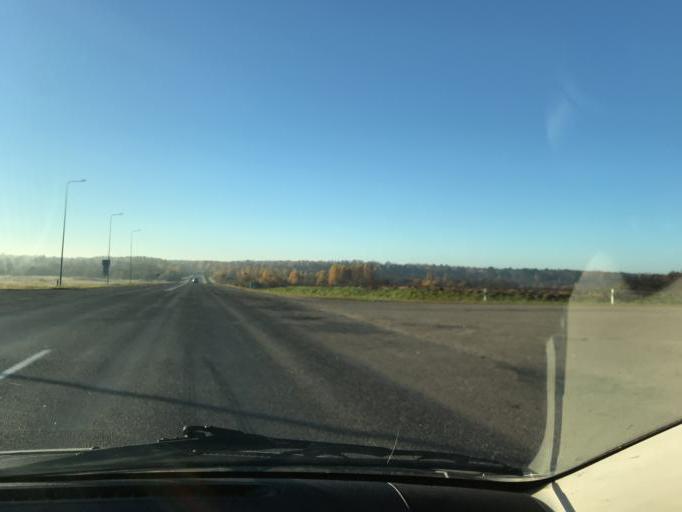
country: BY
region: Vitebsk
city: Vitebsk
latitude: 54.9096
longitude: 30.3759
